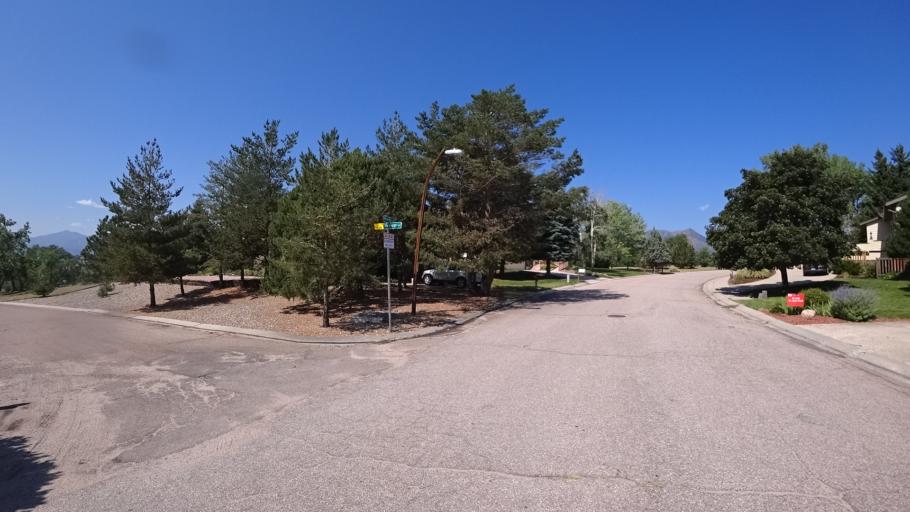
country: US
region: Colorado
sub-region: El Paso County
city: Air Force Academy
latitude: 38.9248
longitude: -104.8261
